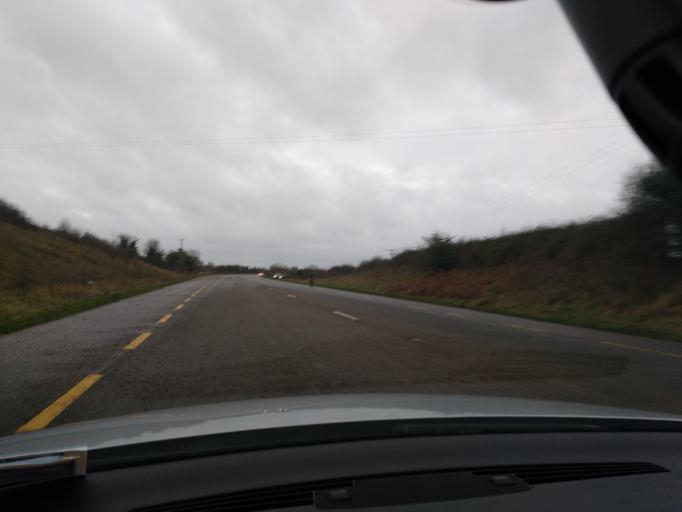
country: IE
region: Munster
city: Thurles
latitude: 52.6808
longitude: -7.6688
